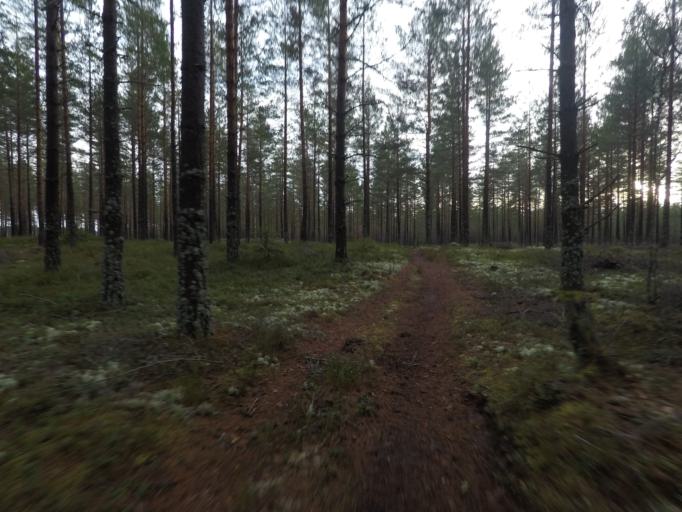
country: SE
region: Vaestmanland
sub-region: Kungsors Kommun
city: Kungsoer
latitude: 59.3510
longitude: 16.1191
